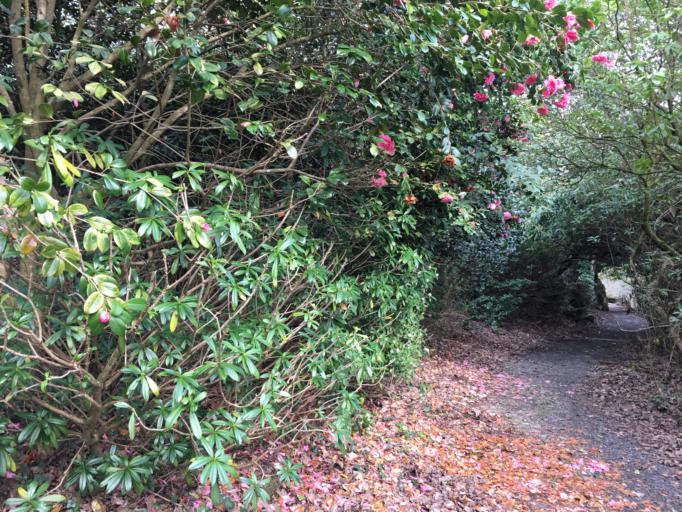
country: GB
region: Wales
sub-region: Gwynedd
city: Porthmadog
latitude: 52.9105
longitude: -4.1019
